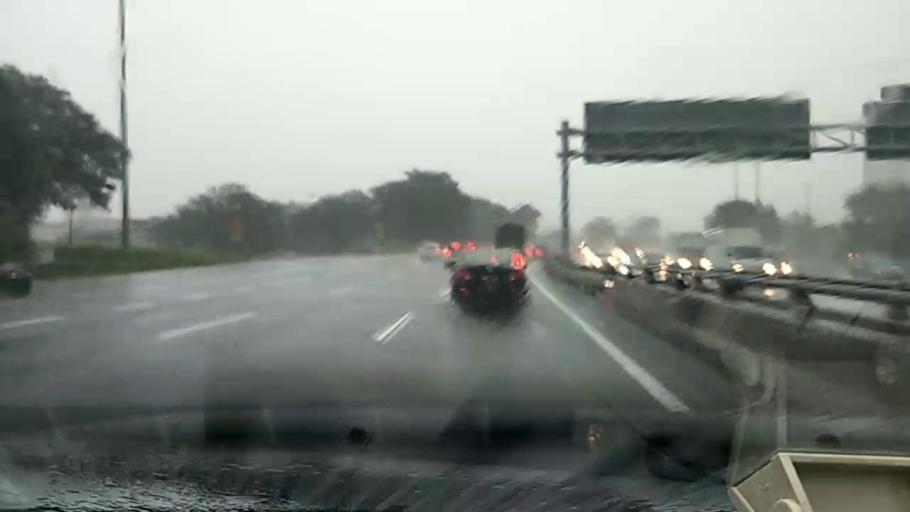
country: MY
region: Selangor
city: Kampong Baharu Balakong
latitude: 2.9809
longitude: 101.7328
